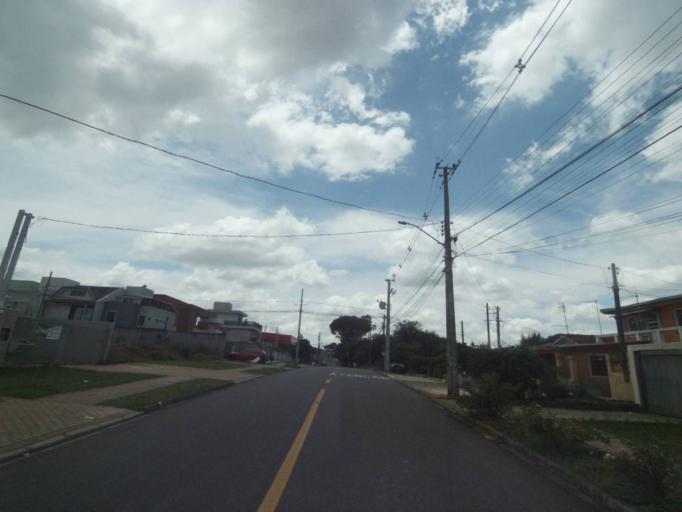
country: BR
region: Parana
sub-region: Curitiba
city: Curitiba
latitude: -25.4615
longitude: -49.3480
